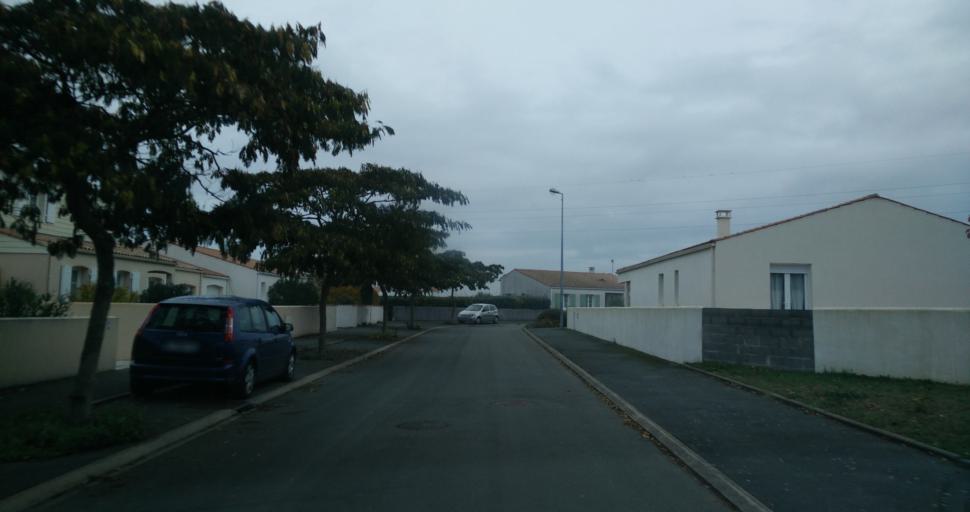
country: FR
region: Poitou-Charentes
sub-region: Departement de la Charente-Maritime
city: Puilboreau
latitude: 46.1853
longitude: -1.1244
